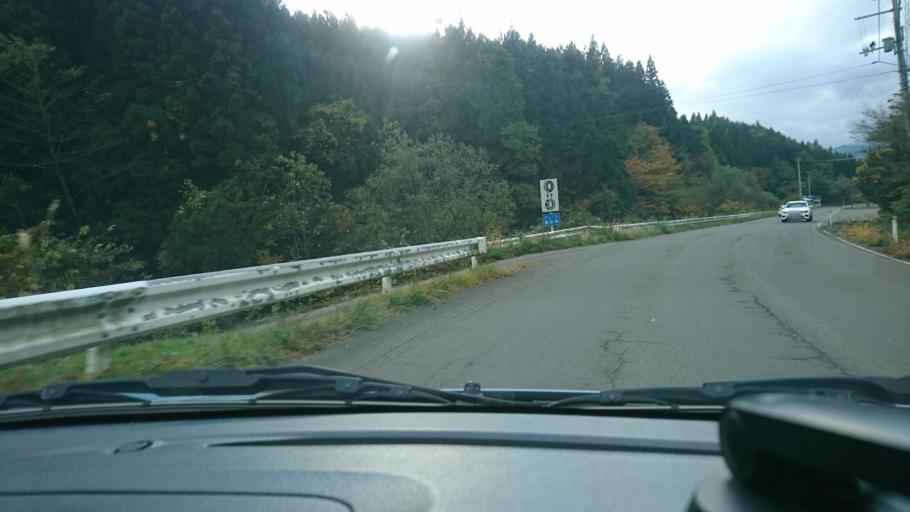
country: JP
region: Miyagi
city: Furukawa
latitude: 38.7402
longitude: 140.7923
